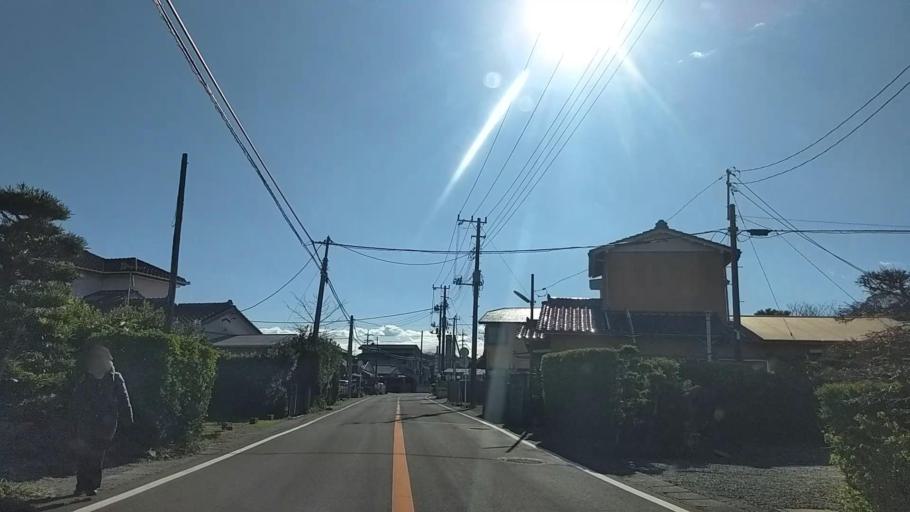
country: JP
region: Chiba
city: Tateyama
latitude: 34.9825
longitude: 139.8623
